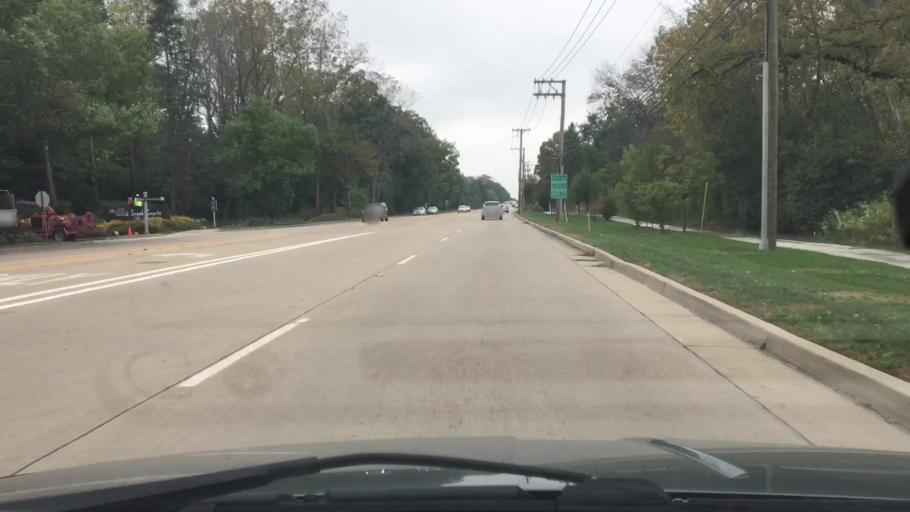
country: US
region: Illinois
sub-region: Lake County
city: Lincolnshire
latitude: 42.2005
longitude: -87.8951
